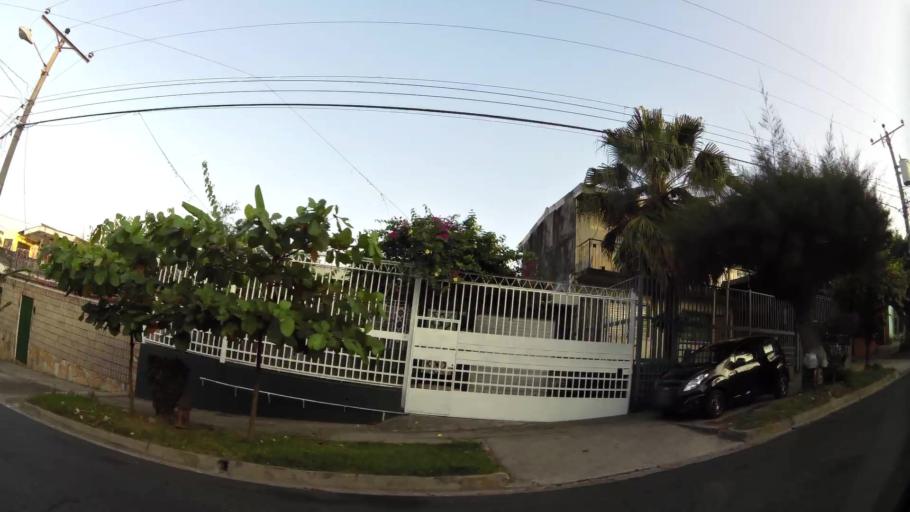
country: SV
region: San Salvador
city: San Salvador
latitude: 13.6825
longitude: -89.2112
